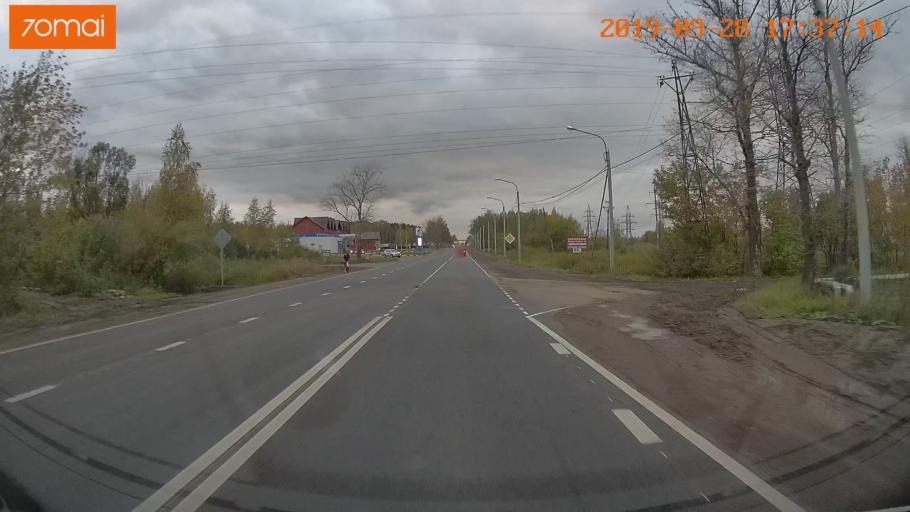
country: RU
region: Jaroslavl
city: Yaroslavl
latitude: 57.5424
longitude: 39.9528
